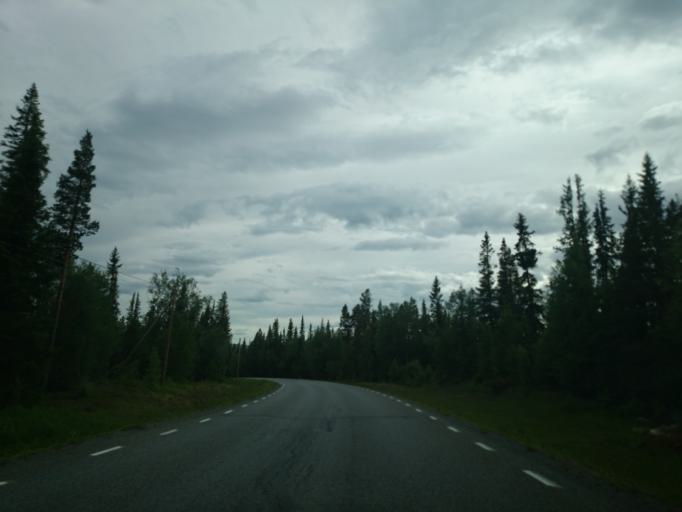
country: SE
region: Jaemtland
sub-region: Are Kommun
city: Are
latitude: 63.2118
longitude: 13.1599
